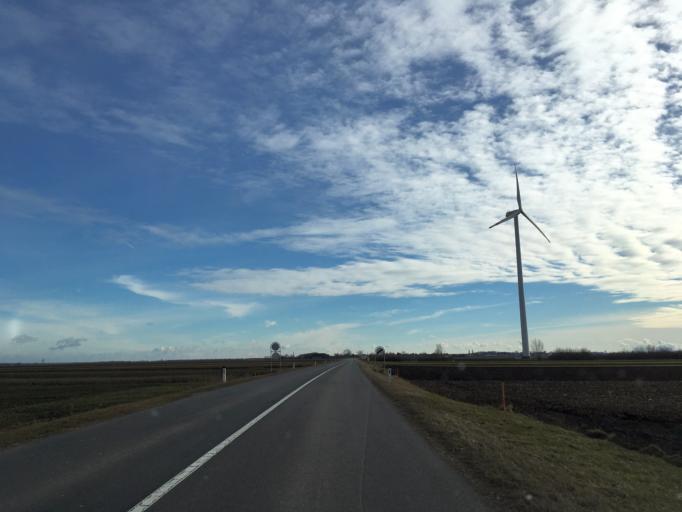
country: AT
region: Burgenland
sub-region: Politischer Bezirk Neusiedl am See
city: Pama
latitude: 48.0621
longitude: 17.0083
